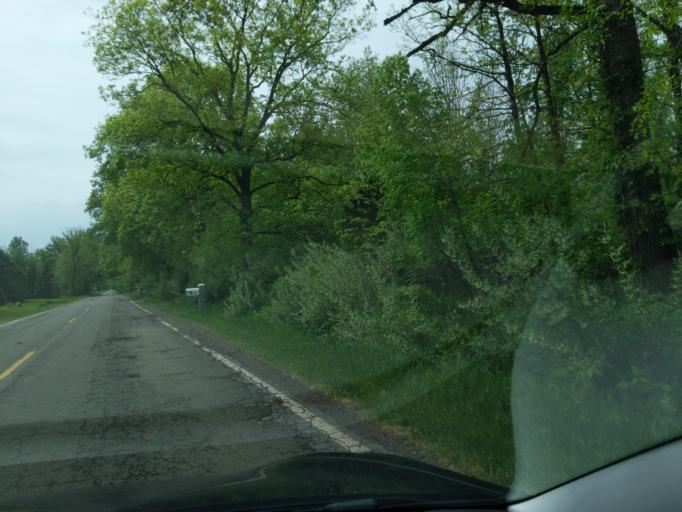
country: US
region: Michigan
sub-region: Ingham County
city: Stockbridge
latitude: 42.4248
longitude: -84.2516
